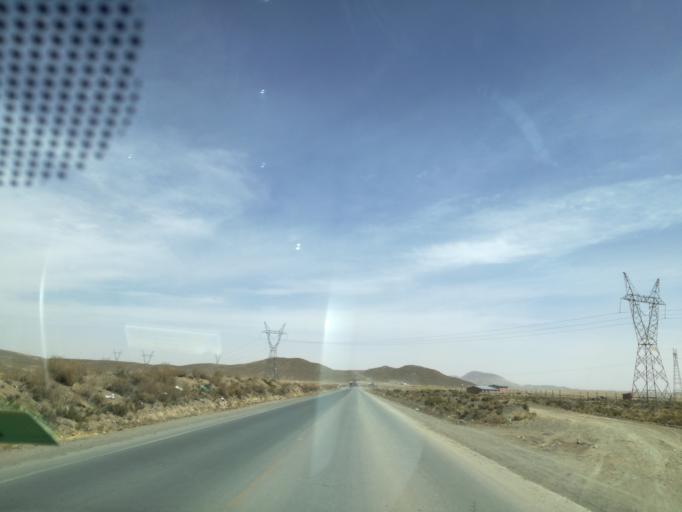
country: BO
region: Oruro
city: Oruro
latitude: -17.8775
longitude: -67.0240
